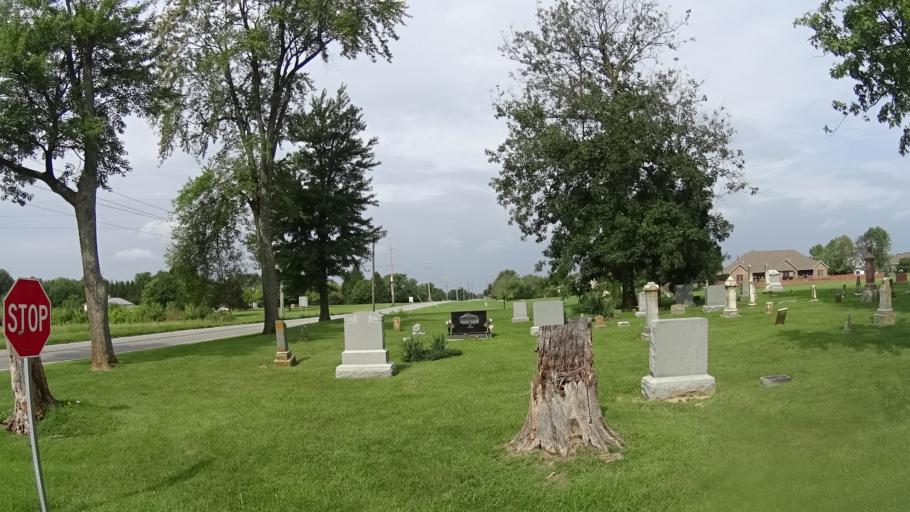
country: US
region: Indiana
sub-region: Madison County
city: Pendleton
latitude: 40.0098
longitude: -85.7914
